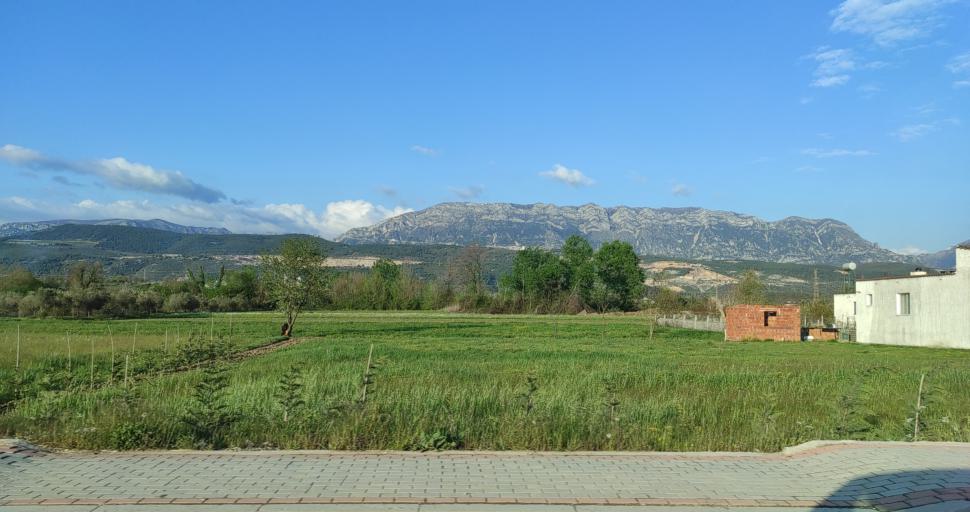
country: AL
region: Durres
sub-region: Rrethi i Krujes
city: Fushe-Kruje
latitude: 41.4892
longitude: 19.7246
